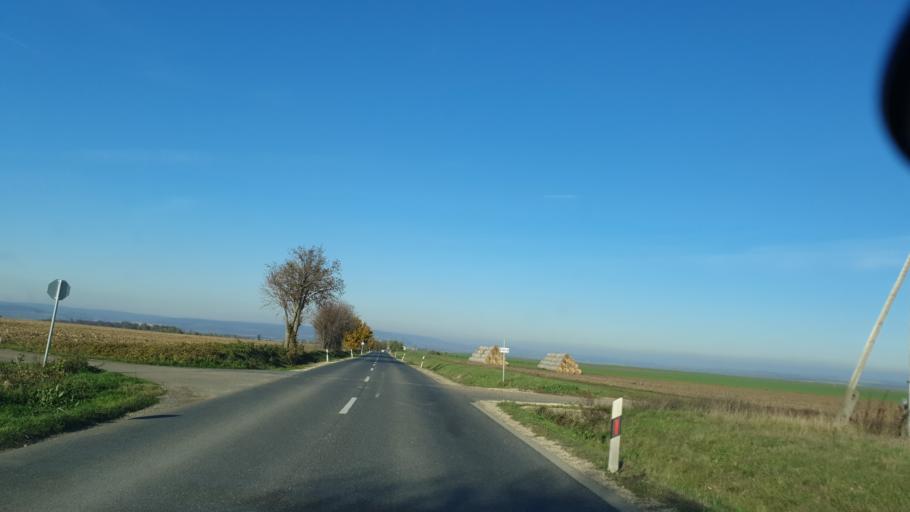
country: HU
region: Fejer
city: Zamoly
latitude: 47.2869
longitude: 18.4214
